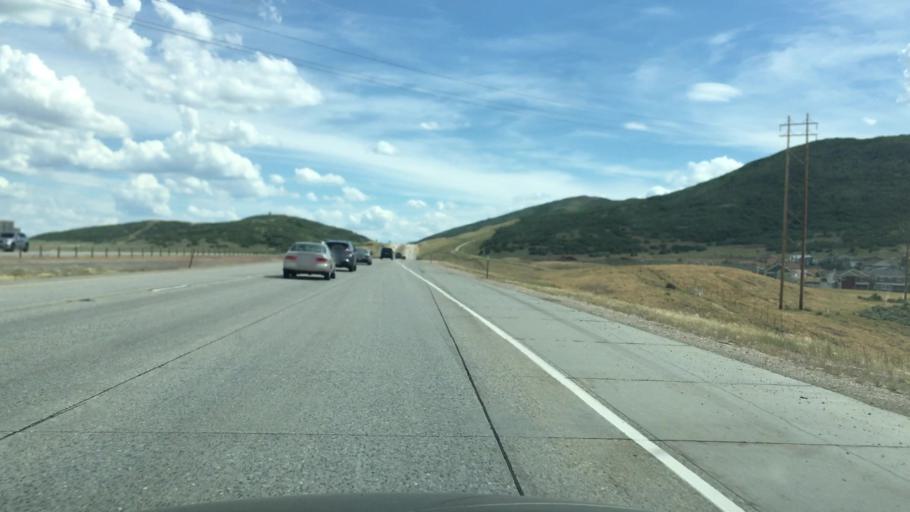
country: US
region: Utah
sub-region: Summit County
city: Park City
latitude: 40.6766
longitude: -111.4604
